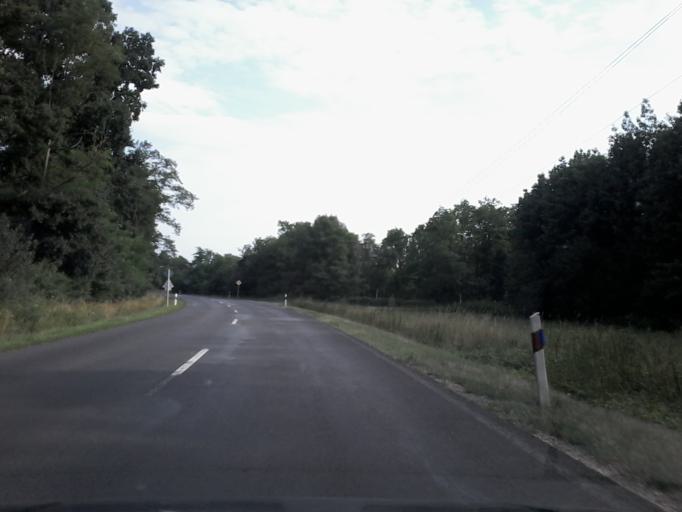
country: HU
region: Vas
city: Sarvar
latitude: 47.1773
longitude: 17.0305
